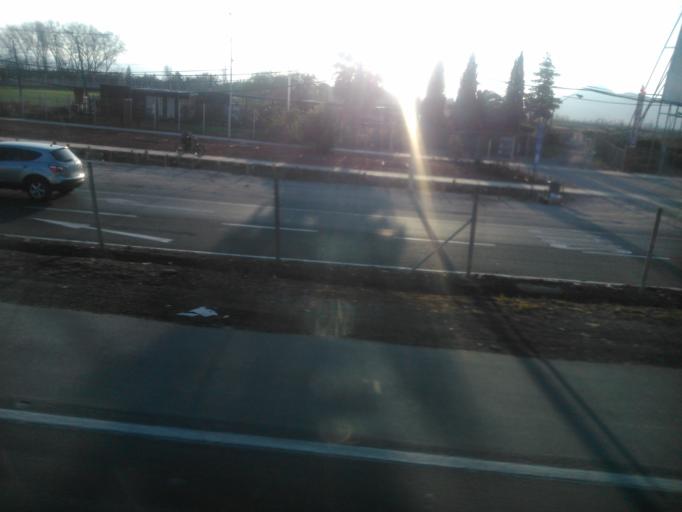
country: CL
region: Santiago Metropolitan
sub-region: Provincia de Maipo
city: Buin
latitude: -33.7589
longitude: -70.7413
